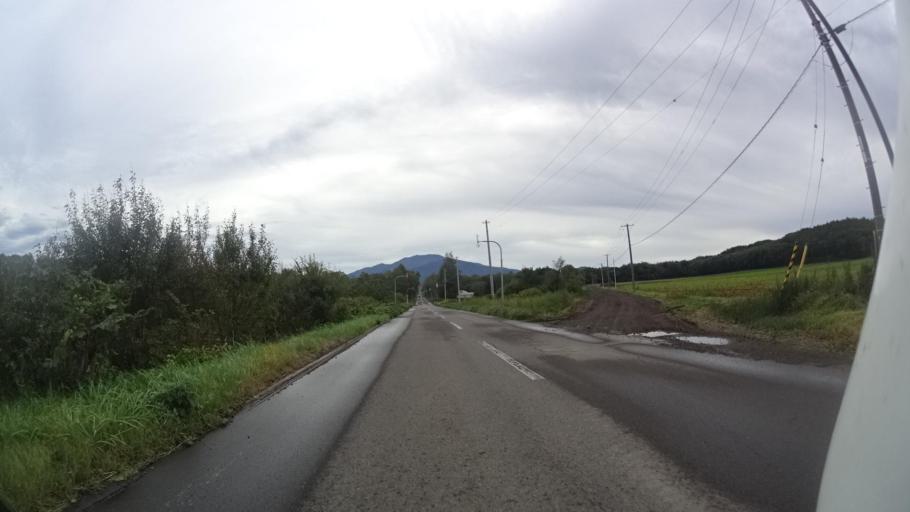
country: JP
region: Hokkaido
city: Shibetsu
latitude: 43.8730
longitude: 144.7158
